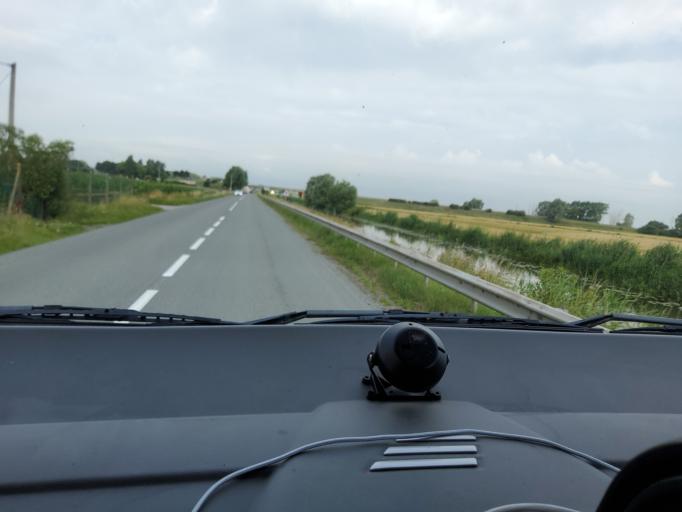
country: FR
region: Nord-Pas-de-Calais
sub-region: Departement du Nord
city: Bourbourg
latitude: 50.9513
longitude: 2.2311
